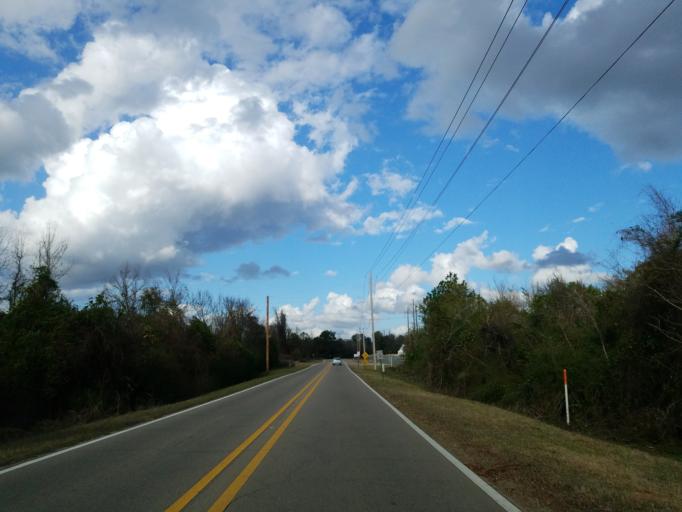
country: US
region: Mississippi
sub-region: Forrest County
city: Glendale
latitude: 31.3524
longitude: -89.3050
